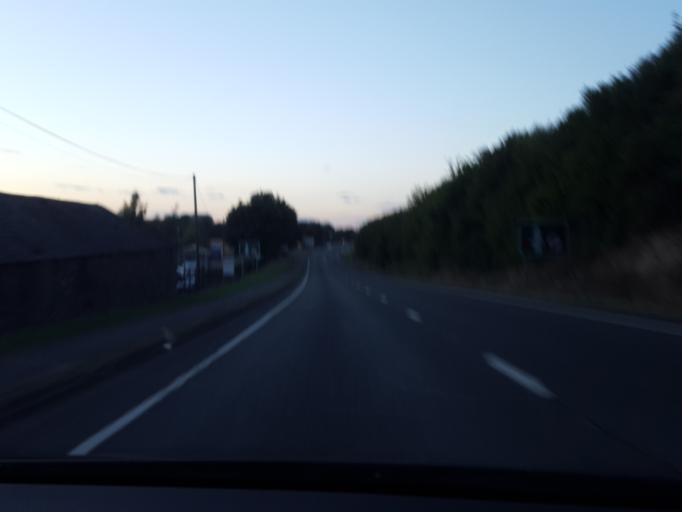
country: GB
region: England
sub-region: Leicestershire
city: Mountsorrel
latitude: 52.6966
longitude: -1.1262
